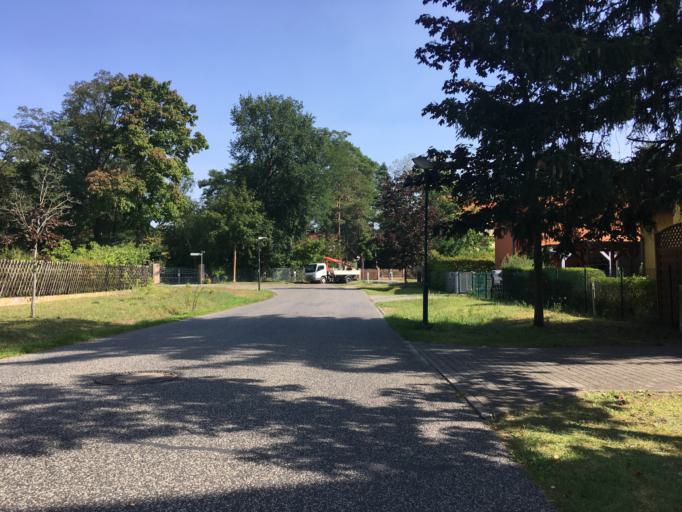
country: DE
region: Brandenburg
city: Zeuthen
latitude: 52.3754
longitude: 13.6303
